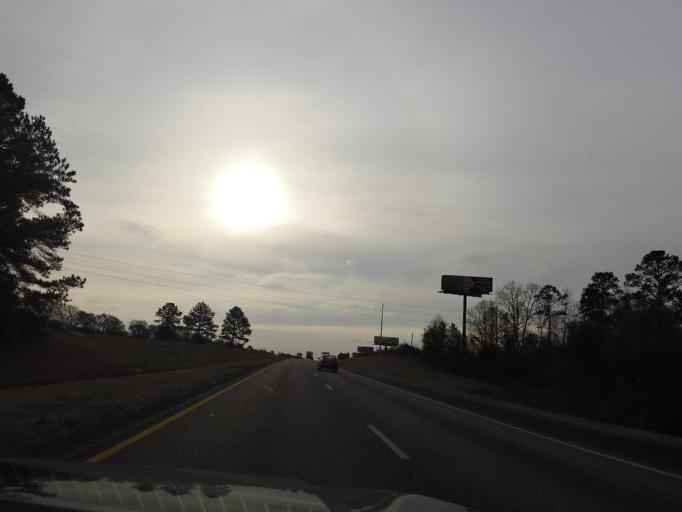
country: US
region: Alabama
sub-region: Autauga County
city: Prattville
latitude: 32.5088
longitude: -86.4243
